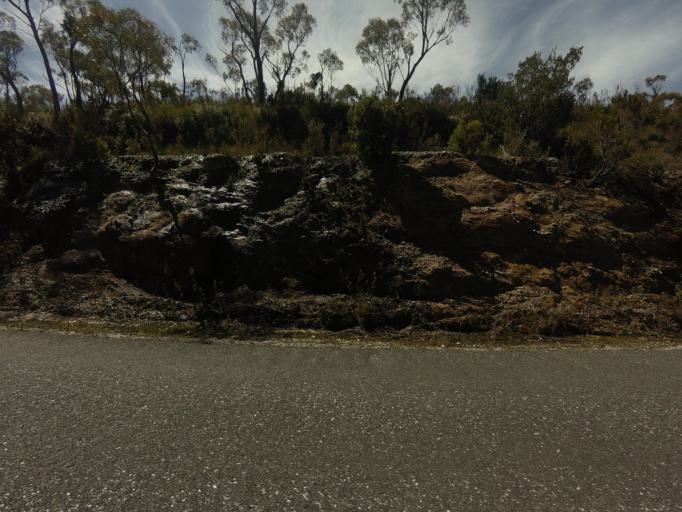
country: AU
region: Tasmania
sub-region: West Coast
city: Queenstown
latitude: -42.7798
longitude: 146.0575
